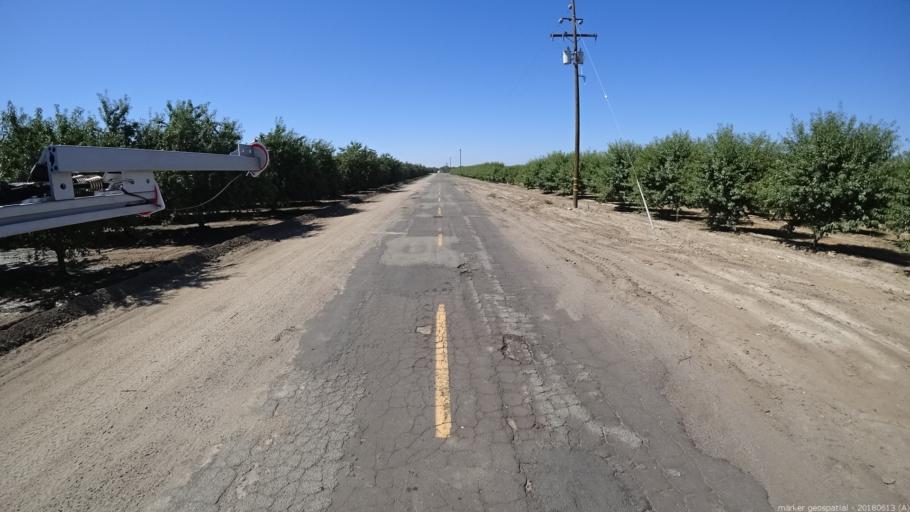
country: US
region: California
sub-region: Madera County
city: Chowchilla
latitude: 37.0578
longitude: -120.4192
